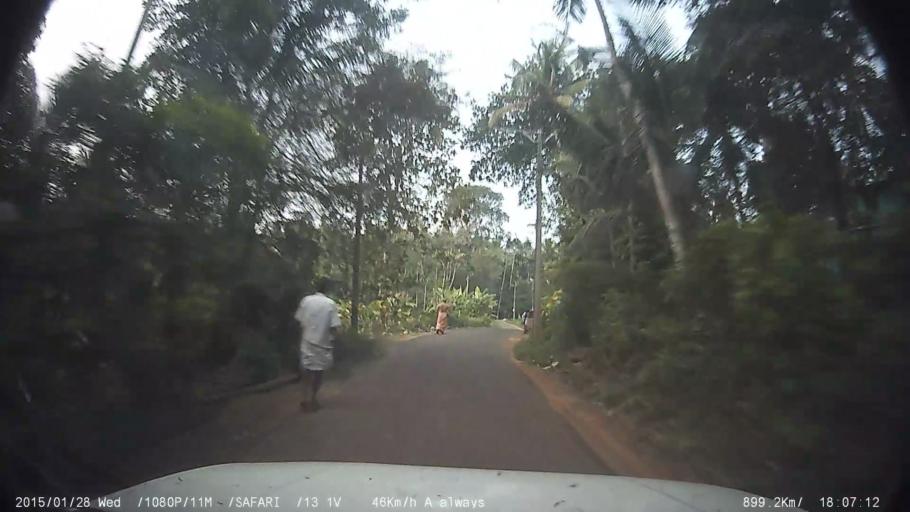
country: IN
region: Kerala
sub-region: Kottayam
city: Palackattumala
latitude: 9.7336
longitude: 76.5772
